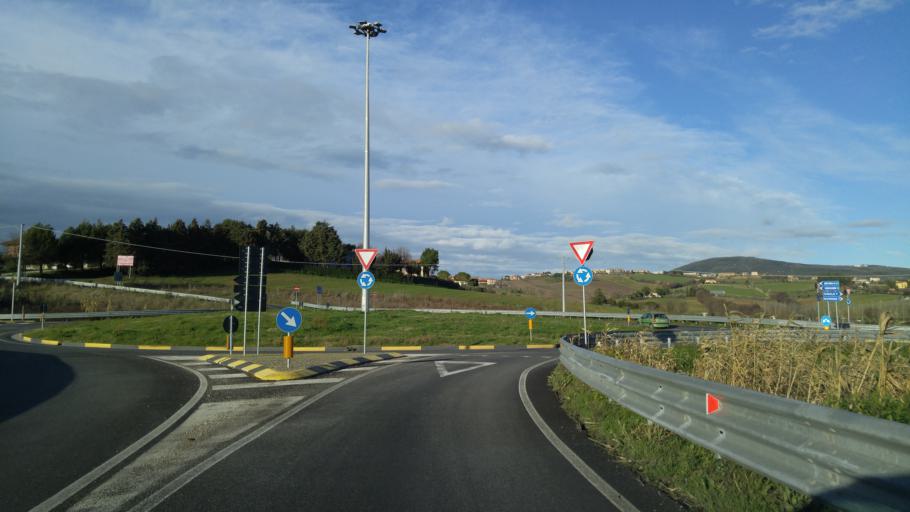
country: IT
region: The Marches
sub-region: Provincia di Ancona
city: Camerano
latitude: 43.5066
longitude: 13.5467
